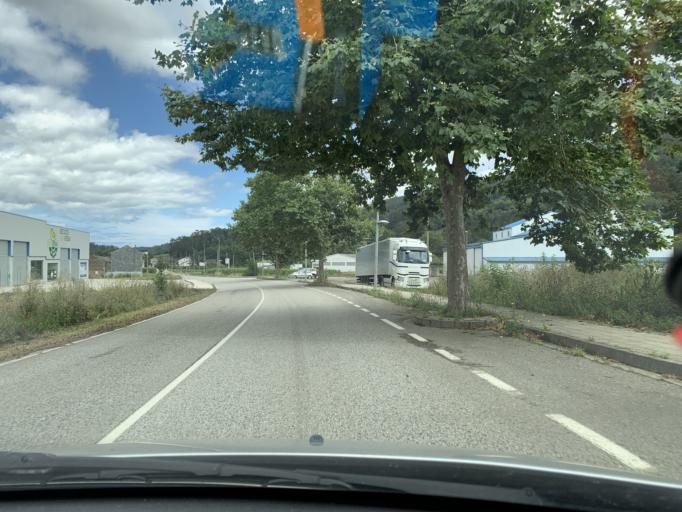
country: ES
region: Galicia
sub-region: Provincia de Lugo
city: Mondonedo
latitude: 43.4365
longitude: -7.3583
